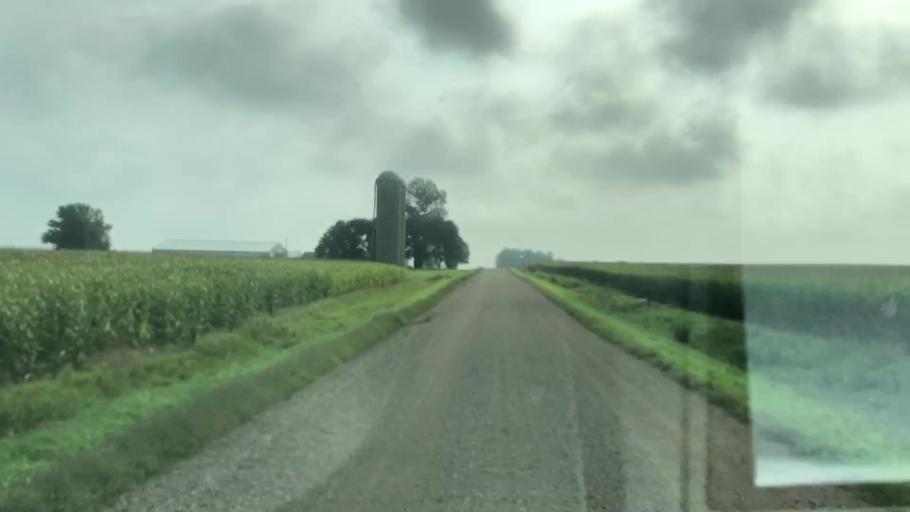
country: US
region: Iowa
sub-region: Sioux County
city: Hull
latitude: 43.2297
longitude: -96.0657
